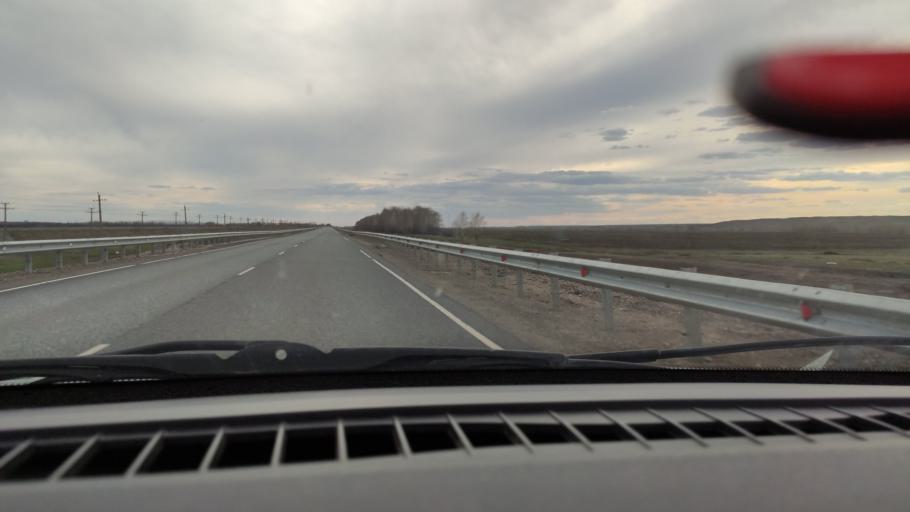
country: RU
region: Bashkortostan
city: Mayachnyy
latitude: 52.4127
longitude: 55.7517
